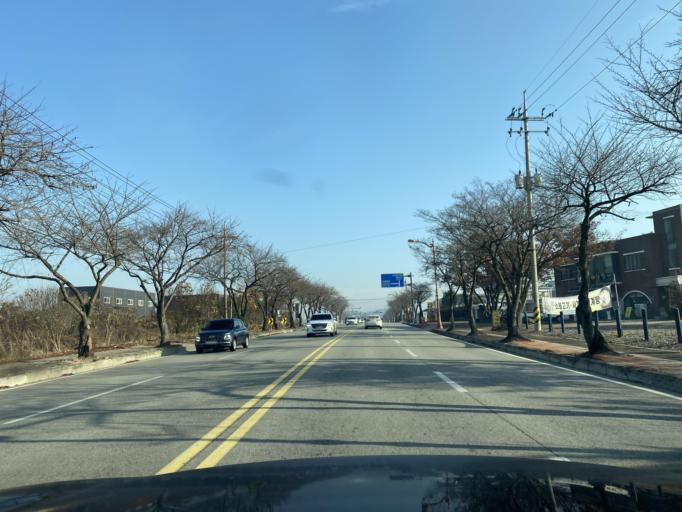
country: KR
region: Chungcheongnam-do
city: Yesan
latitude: 36.7219
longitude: 126.8483
